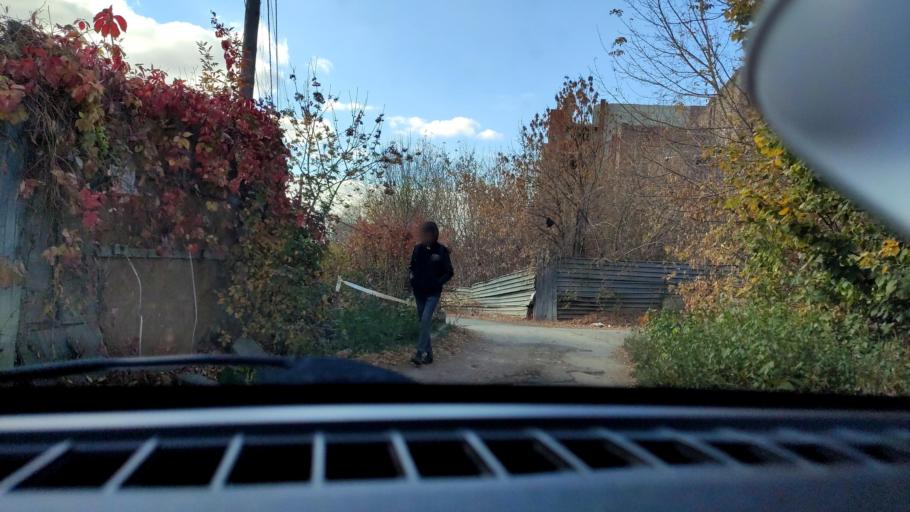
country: RU
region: Samara
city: Samara
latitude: 53.2217
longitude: 50.1790
